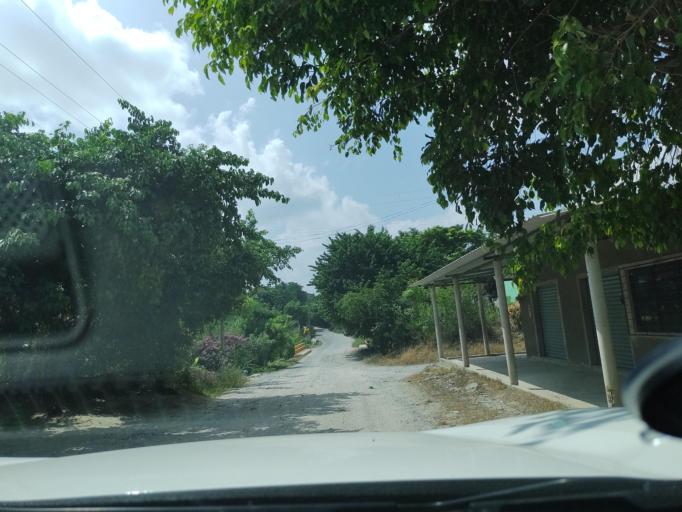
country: MX
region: Veracruz
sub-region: Martinez de la Torre
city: La Union Paso Largo
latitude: 20.1830
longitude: -97.0337
